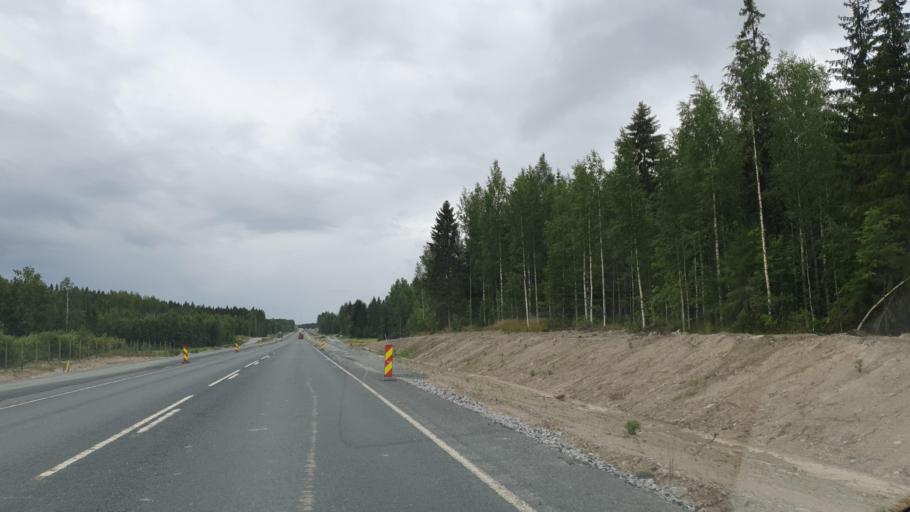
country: FI
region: Northern Savo
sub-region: Ylae-Savo
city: Lapinlahti
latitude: 63.3012
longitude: 27.4515
